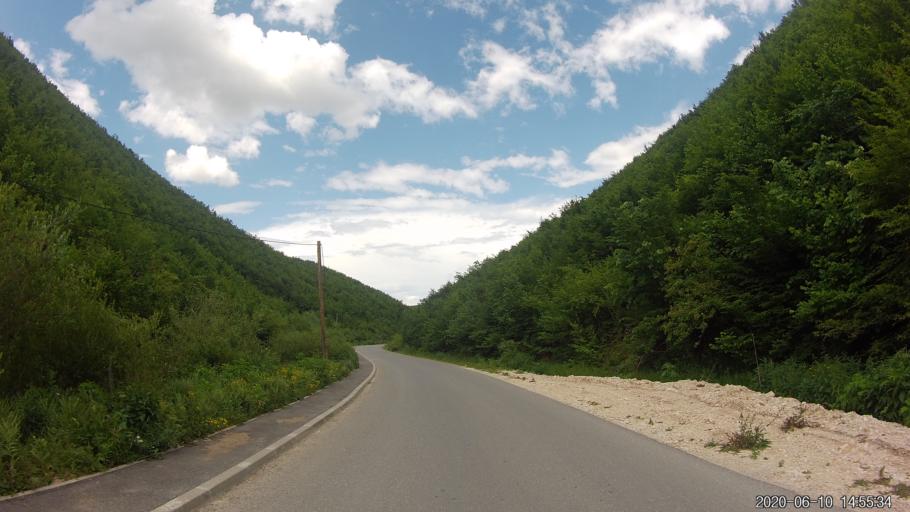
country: XK
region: Ferizaj
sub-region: Komuna e Shtimes
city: Shtime
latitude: 42.4082
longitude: 20.9982
